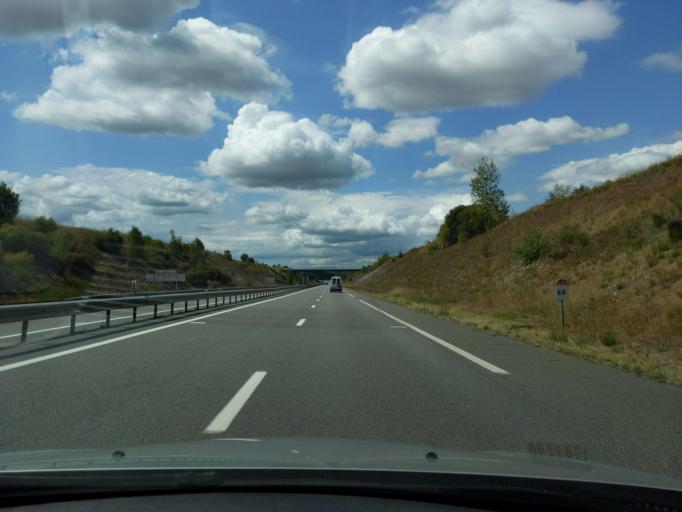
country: FR
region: Limousin
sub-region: Departement de la Creuse
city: Gouzon
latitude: 46.1945
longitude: 2.1653
